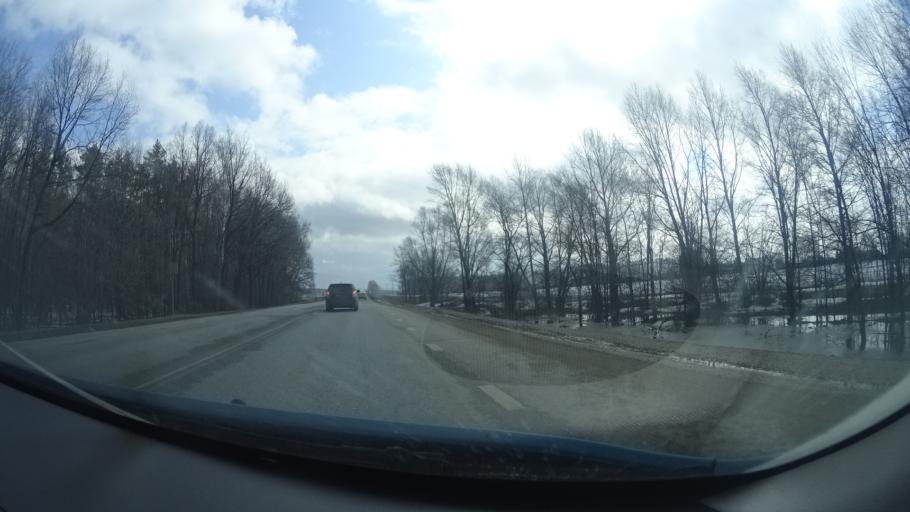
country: RU
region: Bashkortostan
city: Mikhaylovka
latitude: 54.8389
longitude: 55.7969
